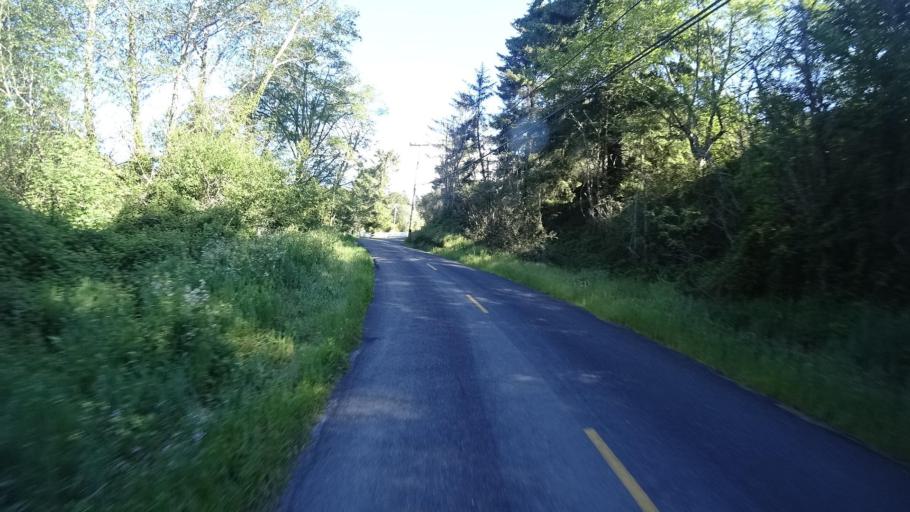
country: US
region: California
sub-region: Humboldt County
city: McKinleyville
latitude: 40.9952
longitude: -124.0991
